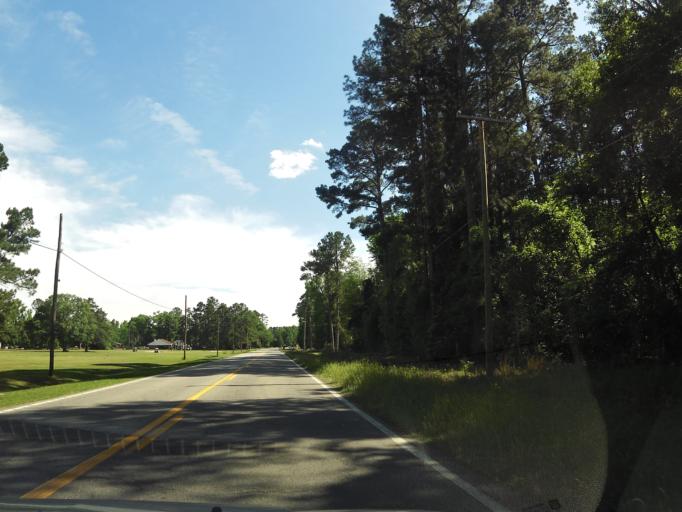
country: US
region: South Carolina
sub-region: Bamberg County
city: Denmark
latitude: 33.2980
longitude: -81.1459
